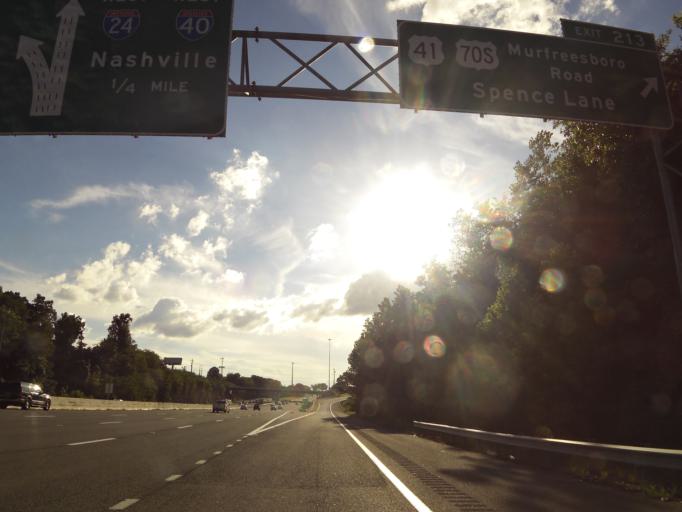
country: US
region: Tennessee
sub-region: Davidson County
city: Nashville
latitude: 36.1413
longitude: -86.7178
